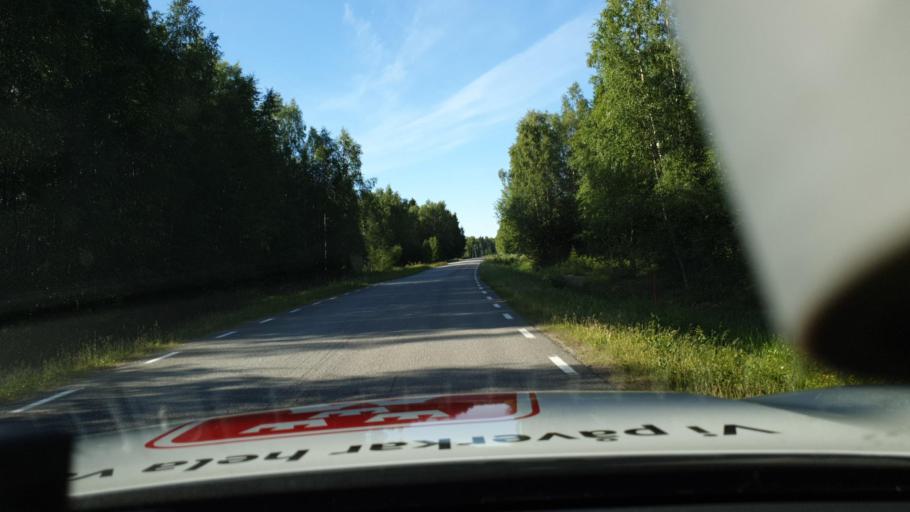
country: SE
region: Norrbotten
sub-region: Kalix Kommun
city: Toere
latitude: 65.8553
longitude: 22.6775
